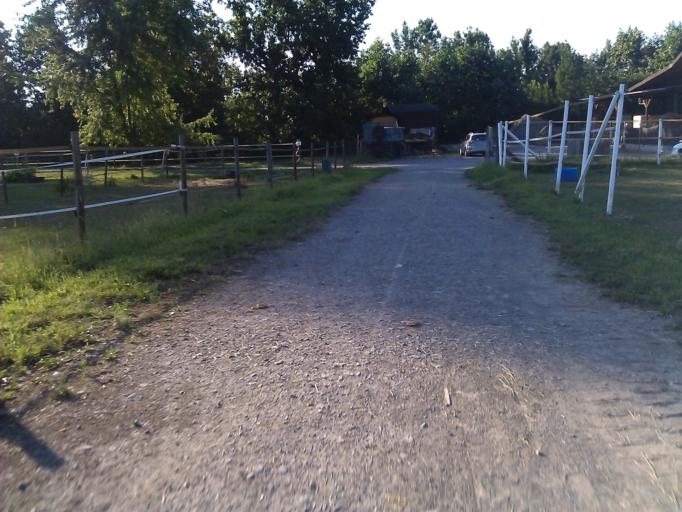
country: DE
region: Baden-Wuerttemberg
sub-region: Regierungsbezirk Stuttgart
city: Untereisesheim
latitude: 49.2238
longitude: 9.2119
